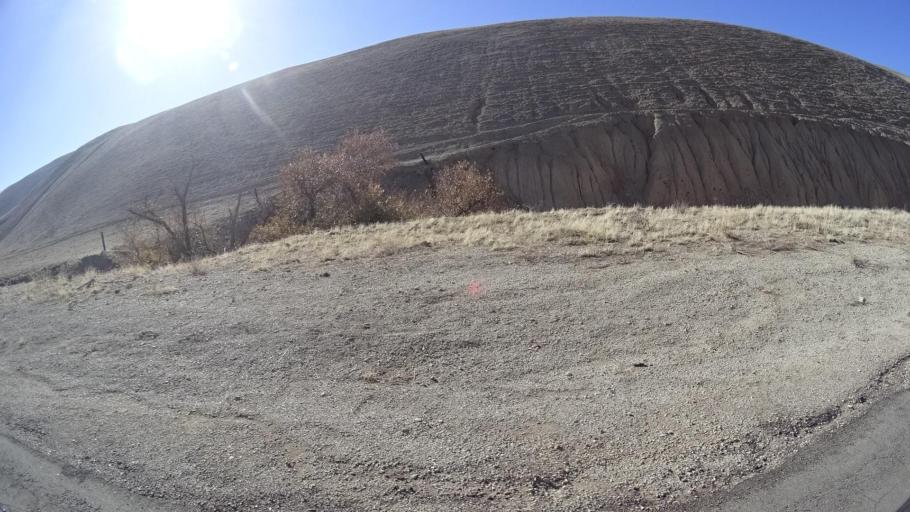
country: US
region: California
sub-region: Kern County
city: Maricopa
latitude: 34.9589
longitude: -119.4100
